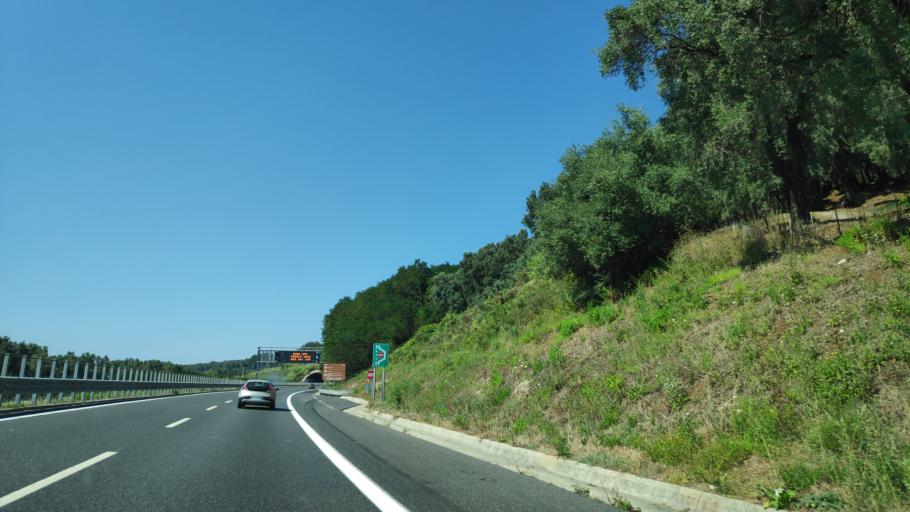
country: IT
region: Calabria
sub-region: Provincia di Reggio Calabria
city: Seminara
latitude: 38.3356
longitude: 15.8613
